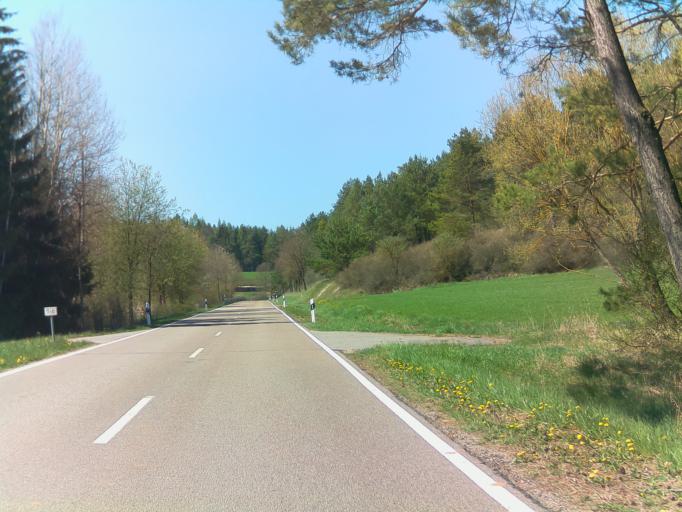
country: DE
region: Bavaria
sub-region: Upper Palatinate
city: Weigendorf
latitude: 49.4581
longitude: 11.5916
